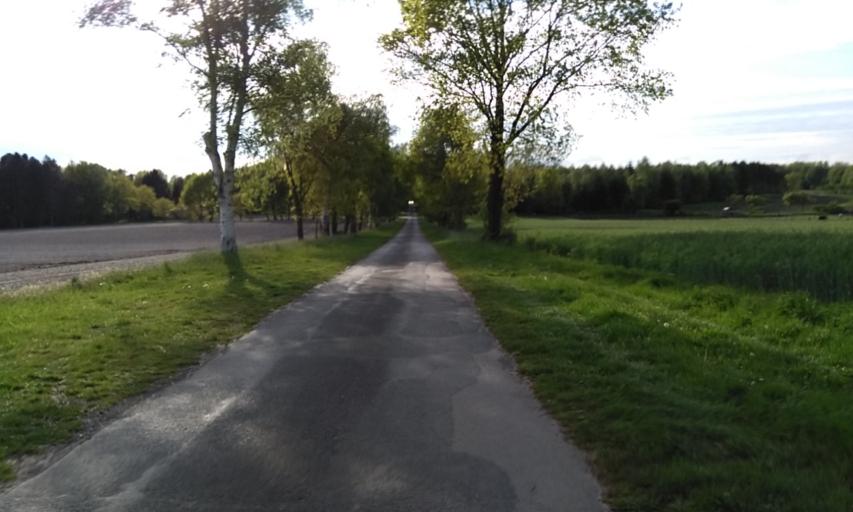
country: DE
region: Lower Saxony
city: Bliedersdorf
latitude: 53.4815
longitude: 9.5620
